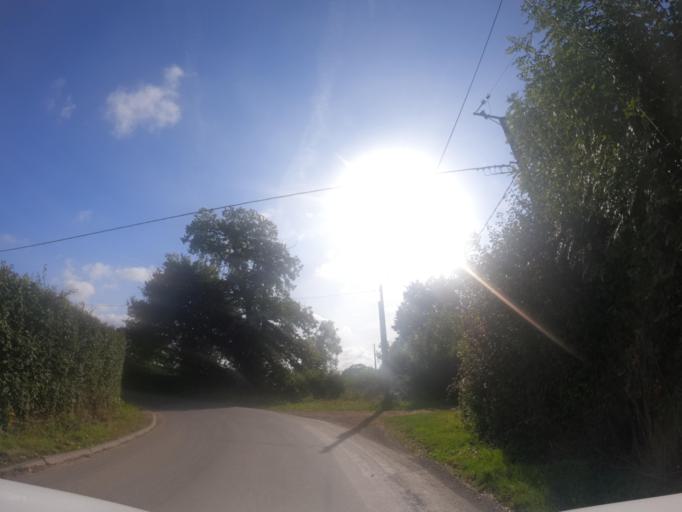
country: FR
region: Poitou-Charentes
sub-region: Departement des Deux-Sevres
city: Courlay
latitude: 46.7748
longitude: -0.5894
